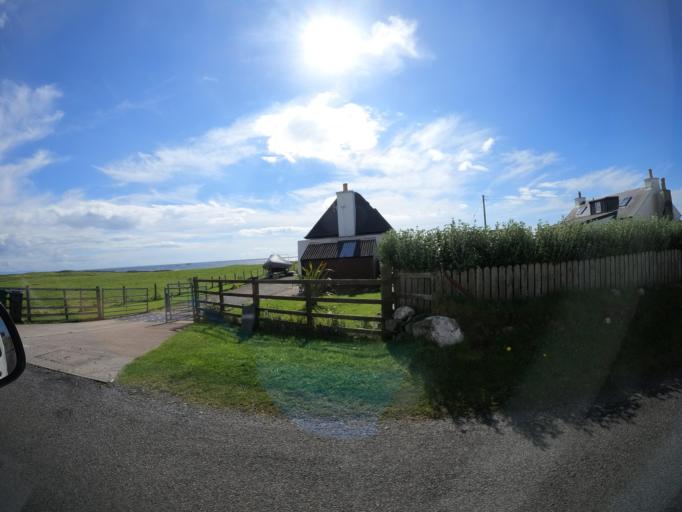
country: GB
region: Scotland
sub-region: Eilean Siar
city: Barra
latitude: 56.4920
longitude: -6.8286
